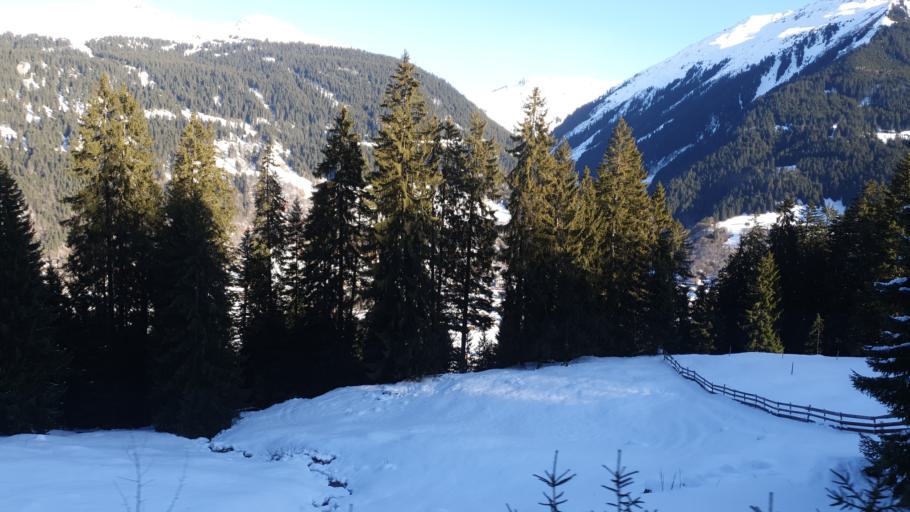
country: CH
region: Grisons
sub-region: Praettigau/Davos District
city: Klosters Serneus
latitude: 46.8726
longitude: 9.8635
